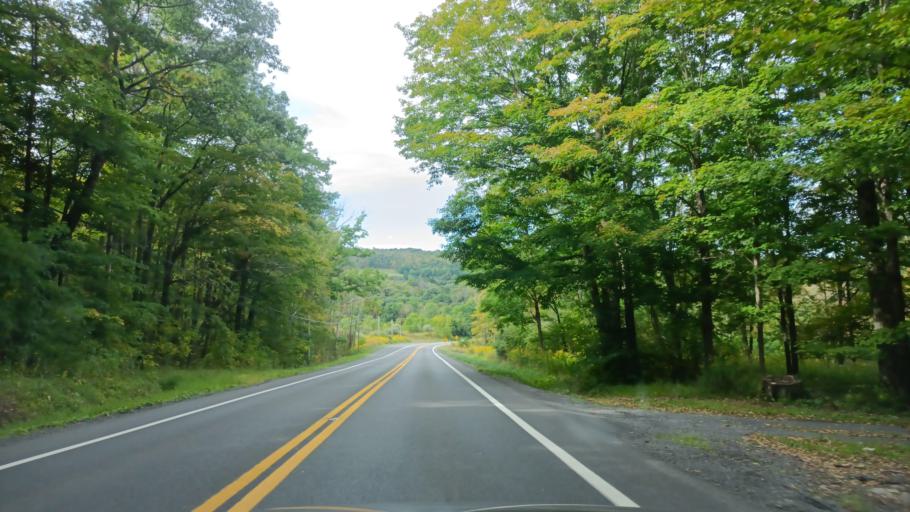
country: US
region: Maryland
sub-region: Garrett County
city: Mountain Lake Park
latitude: 39.2711
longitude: -79.2567
